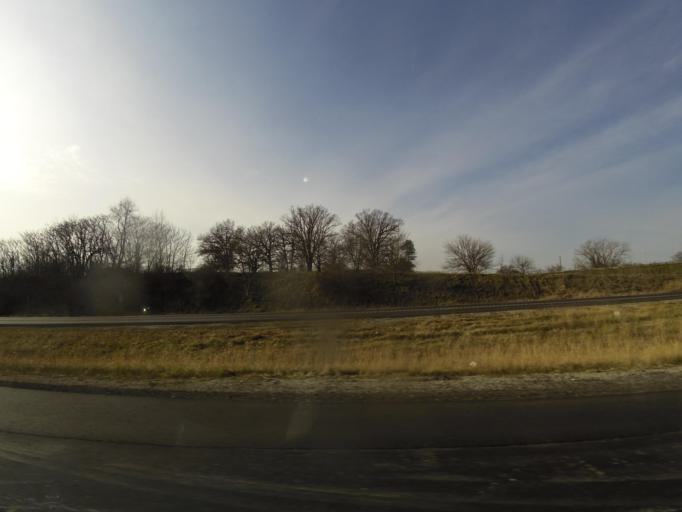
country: US
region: Illinois
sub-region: Macon County
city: Harristown
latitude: 39.8306
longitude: -89.0414
